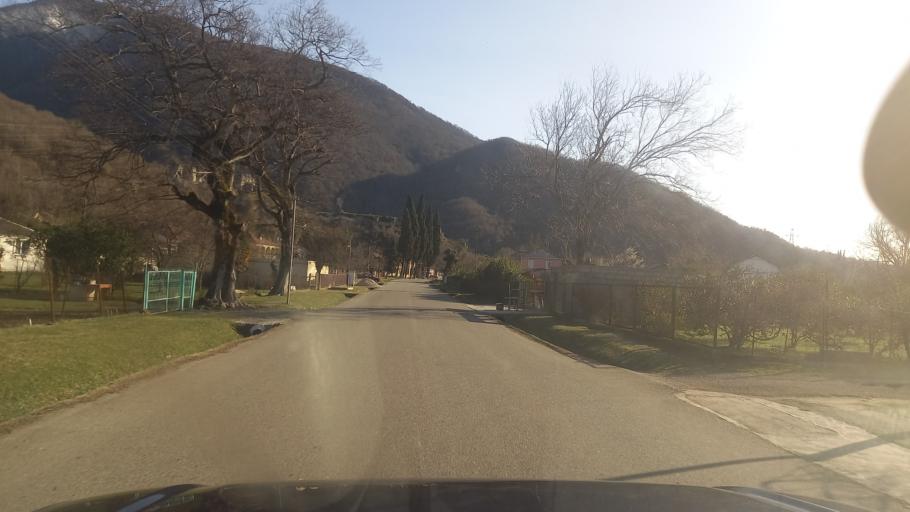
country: GE
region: Abkhazia
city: Bich'vinta
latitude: 43.2388
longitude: 40.3926
